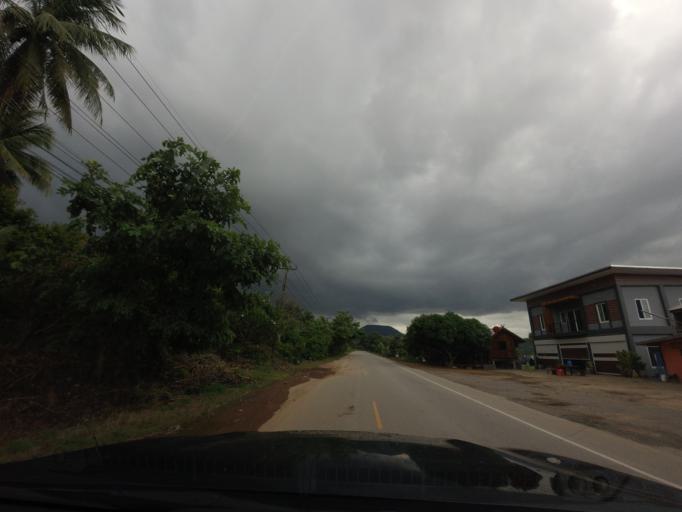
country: LA
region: Vientiane
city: Muang Sanakham
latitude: 17.9607
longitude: 101.7439
